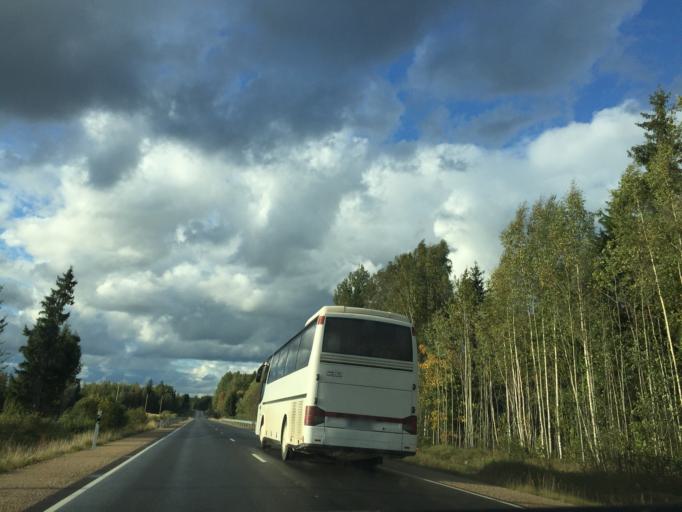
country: LV
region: Ligatne
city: Ligatne
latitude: 57.1454
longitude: 25.0773
